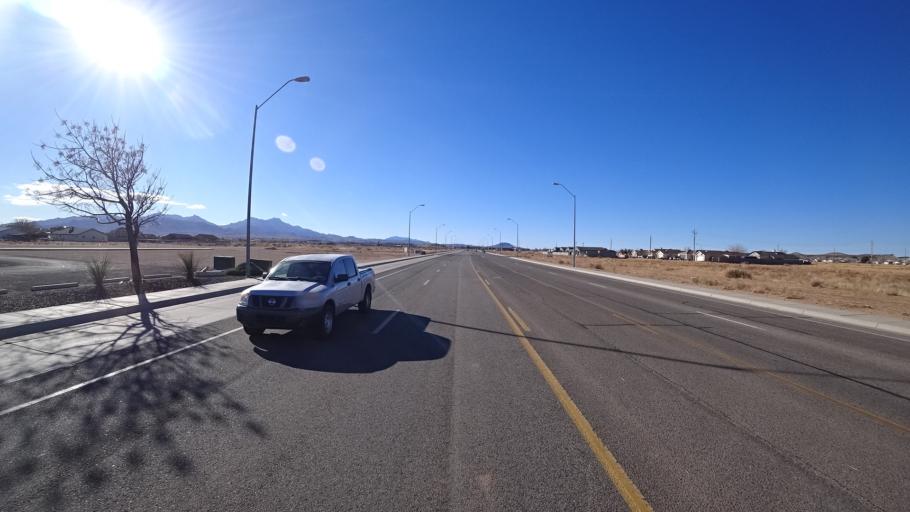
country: US
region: Arizona
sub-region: Mohave County
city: New Kingman-Butler
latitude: 35.2333
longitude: -114.0114
